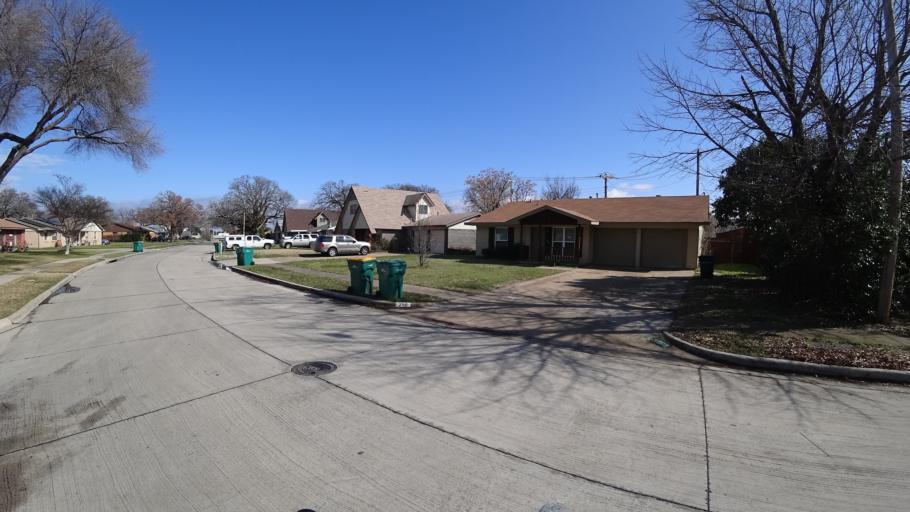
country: US
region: Texas
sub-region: Denton County
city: Lewisville
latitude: 33.0303
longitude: -96.9973
